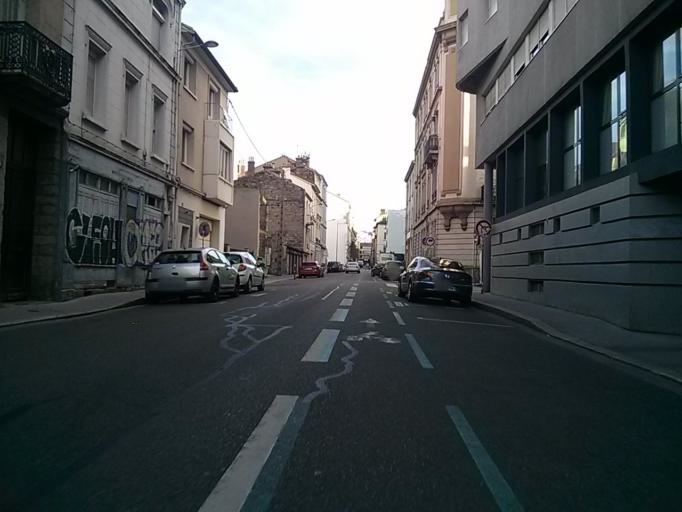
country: FR
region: Rhone-Alpes
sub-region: Departement de la Loire
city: Saint-Etienne
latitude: 45.4448
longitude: 4.3870
